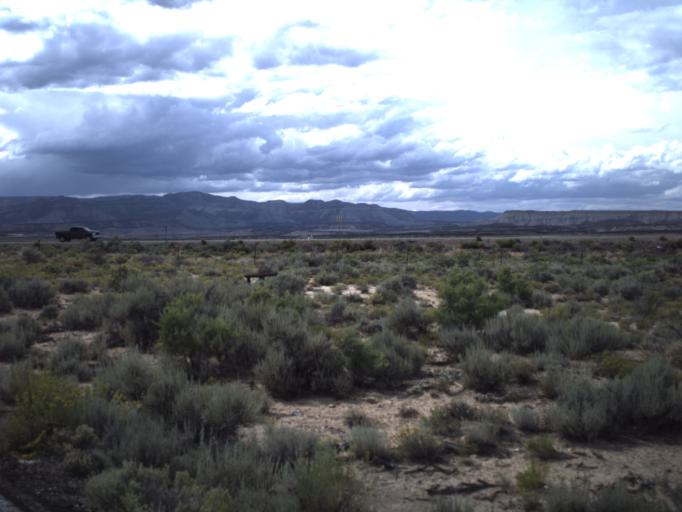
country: US
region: Utah
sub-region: Carbon County
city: Price
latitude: 39.4939
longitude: -110.8436
